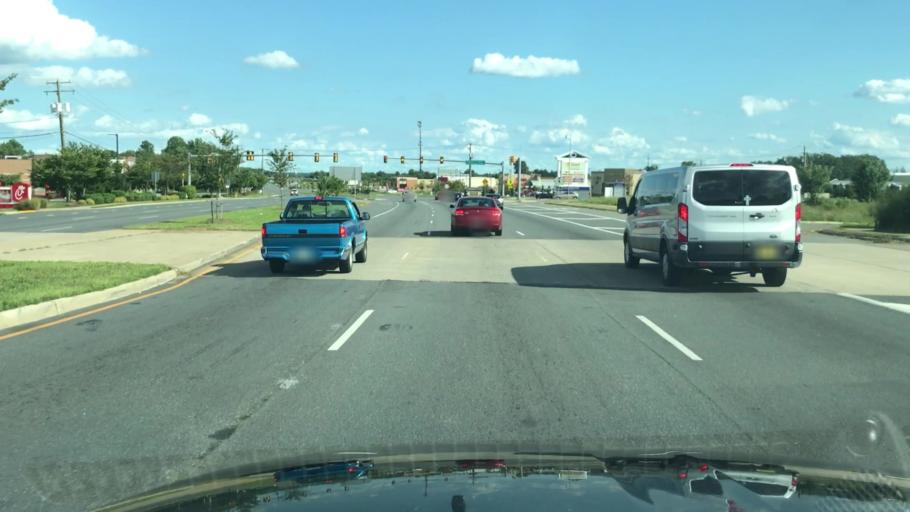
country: US
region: Virginia
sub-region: Stafford County
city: Falmouth
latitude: 38.3596
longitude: -77.5189
